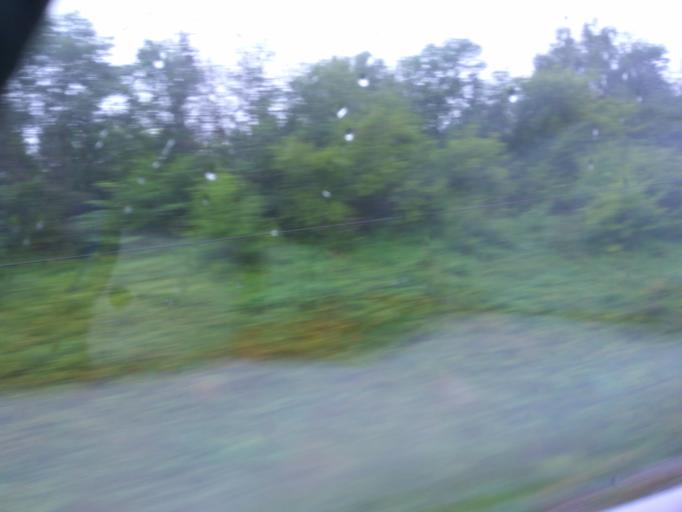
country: RU
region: Moskovskaya
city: Uzunovo
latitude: 54.6288
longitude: 38.5854
